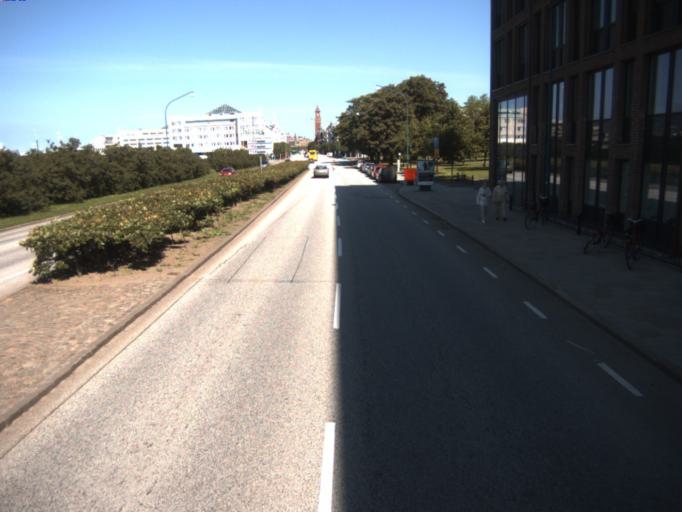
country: SE
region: Skane
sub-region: Helsingborg
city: Helsingborg
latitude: 56.0413
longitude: 12.6980
